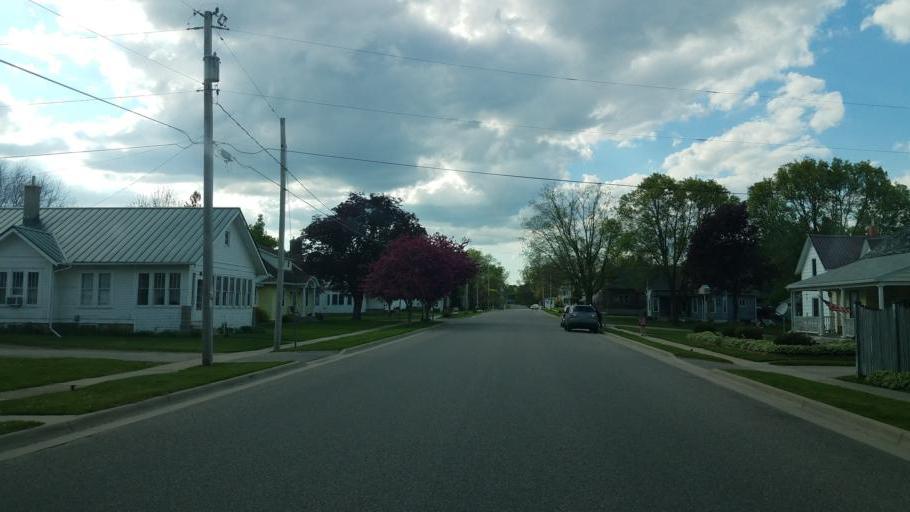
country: US
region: Wisconsin
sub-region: Vernon County
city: Hillsboro
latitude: 43.6534
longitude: -90.3438
